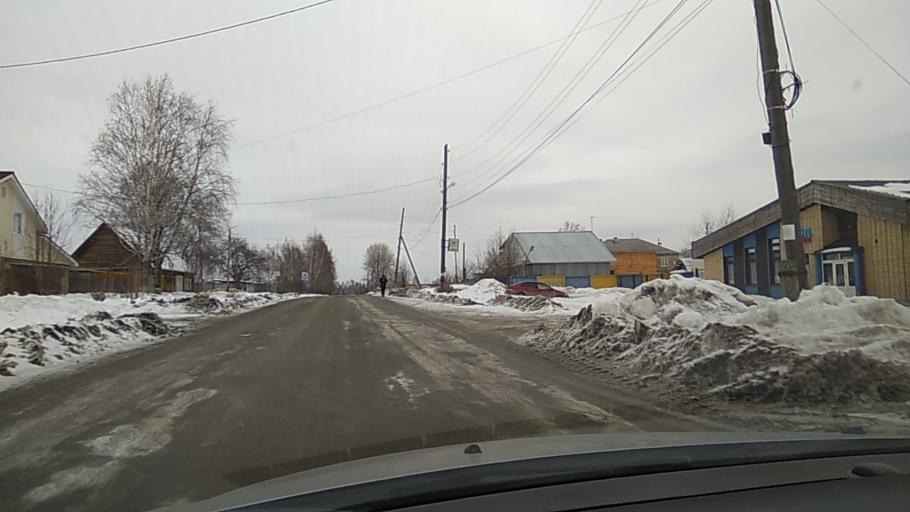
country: RU
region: Sverdlovsk
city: Revda
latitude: 56.8097
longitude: 59.9359
